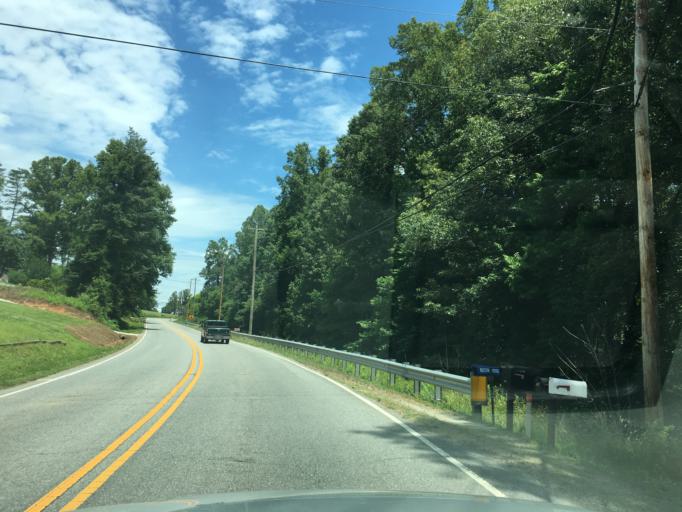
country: US
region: North Carolina
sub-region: Burke County
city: Glen Alpine
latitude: 35.7095
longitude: -81.7629
